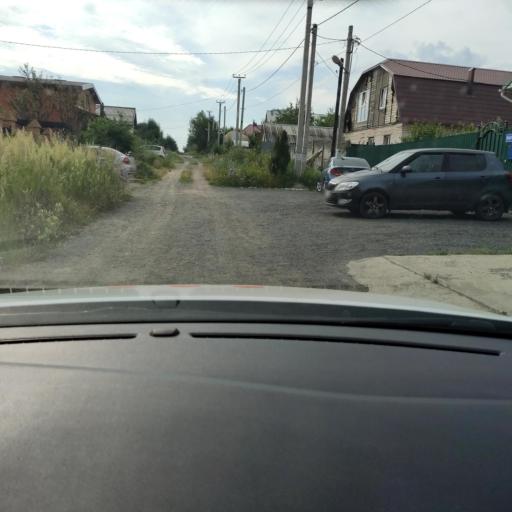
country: RU
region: Tatarstan
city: Stolbishchi
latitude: 55.7597
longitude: 49.2857
